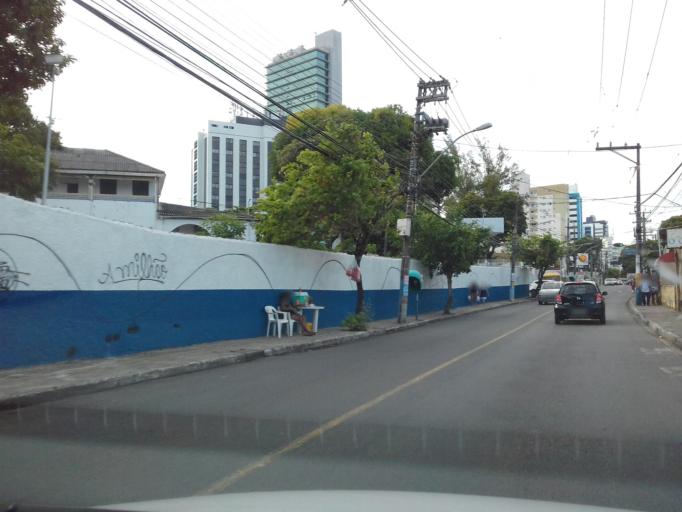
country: BR
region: Bahia
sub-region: Salvador
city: Salvador
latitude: -13.0034
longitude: -38.5005
